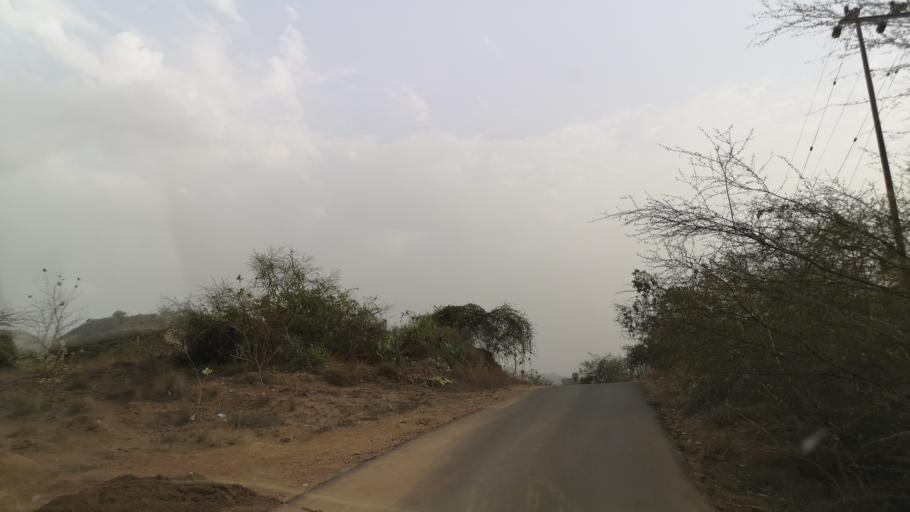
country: YE
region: Sa'dah
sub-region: Monabbih
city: Suq al Khamis
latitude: 17.3777
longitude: 43.1270
